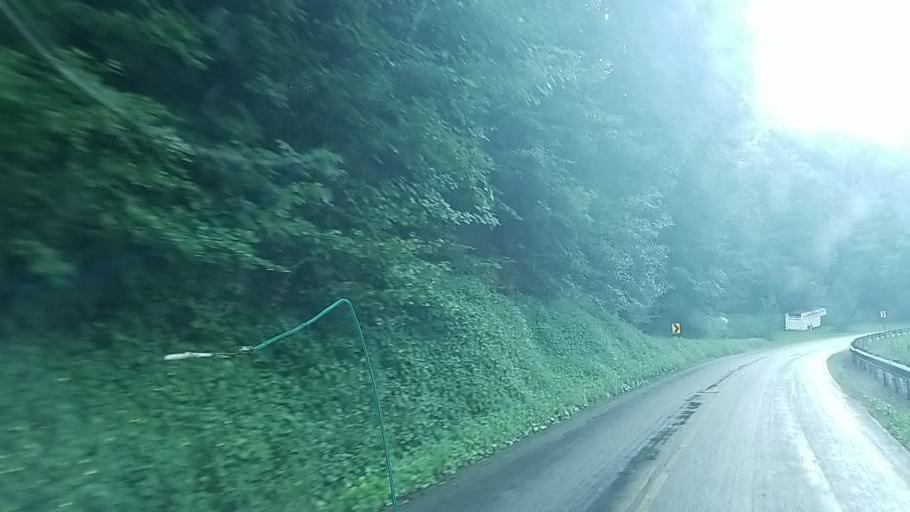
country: US
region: Ohio
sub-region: Wayne County
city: Wooster
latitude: 40.8693
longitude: -82.0231
